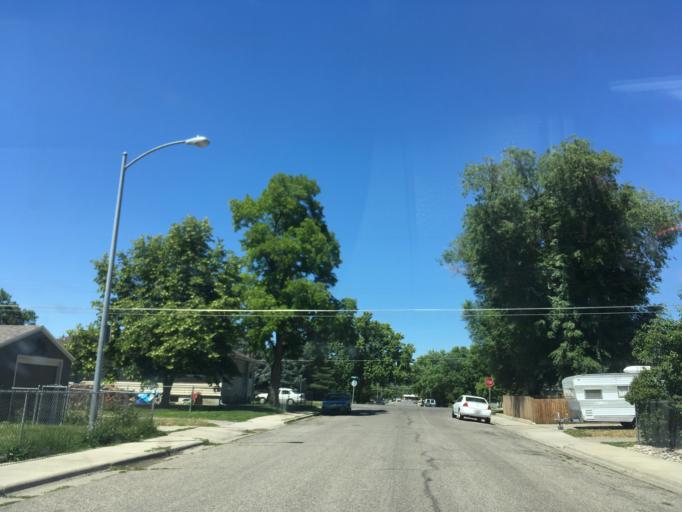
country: US
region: Montana
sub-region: Yellowstone County
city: Billings
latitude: 45.7799
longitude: -108.5616
